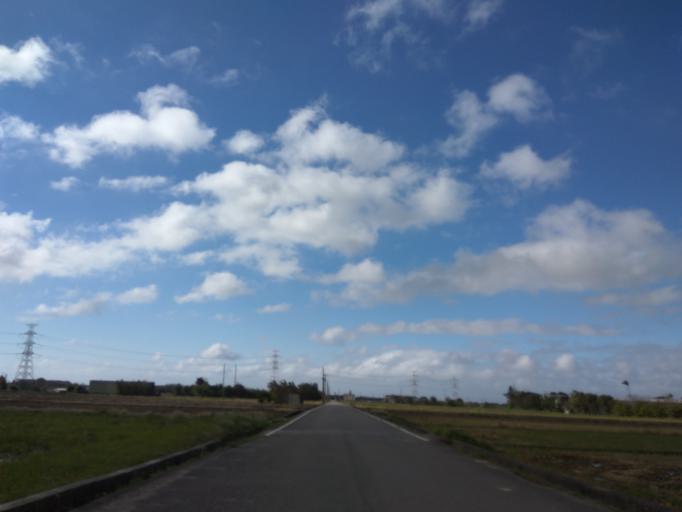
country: TW
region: Taiwan
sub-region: Hsinchu
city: Zhubei
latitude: 24.9704
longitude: 121.0828
